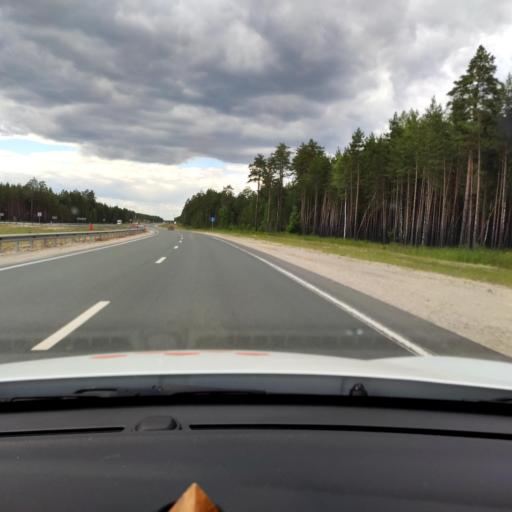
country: RU
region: Mariy-El
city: Surok
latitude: 56.4508
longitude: 48.1015
